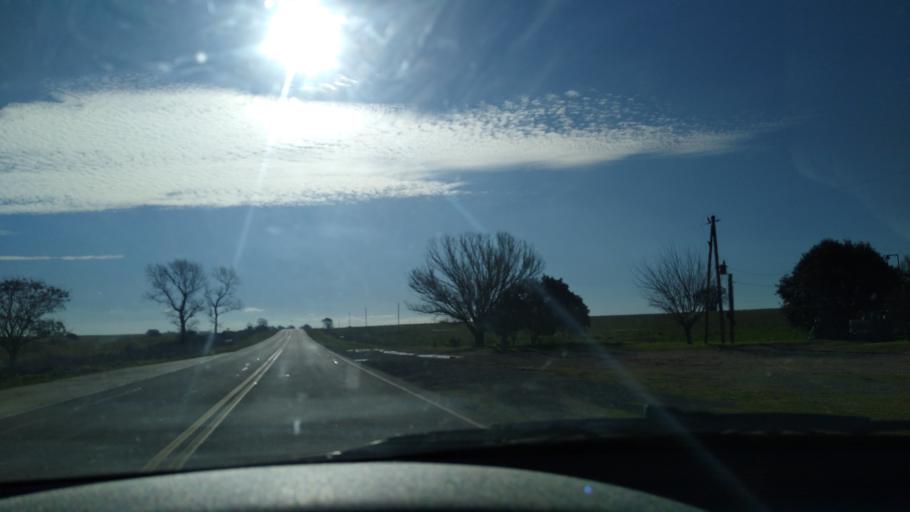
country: AR
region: Entre Rios
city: Aranguren
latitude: -32.3486
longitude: -60.3652
